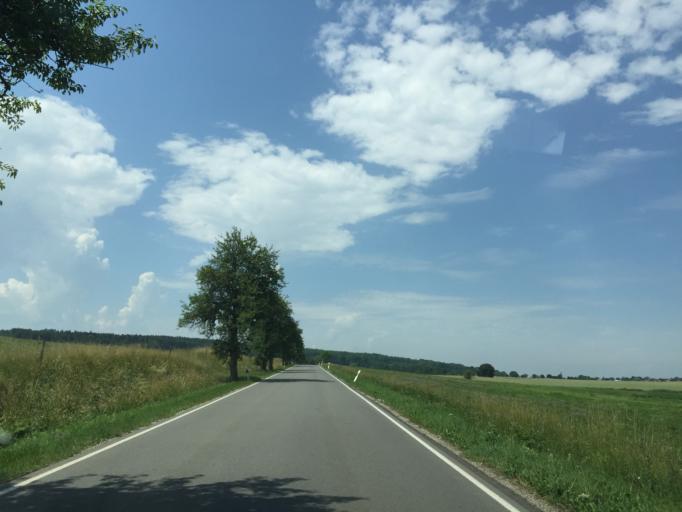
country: DE
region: Thuringia
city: Barchfeld
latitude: 50.8066
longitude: 11.1605
